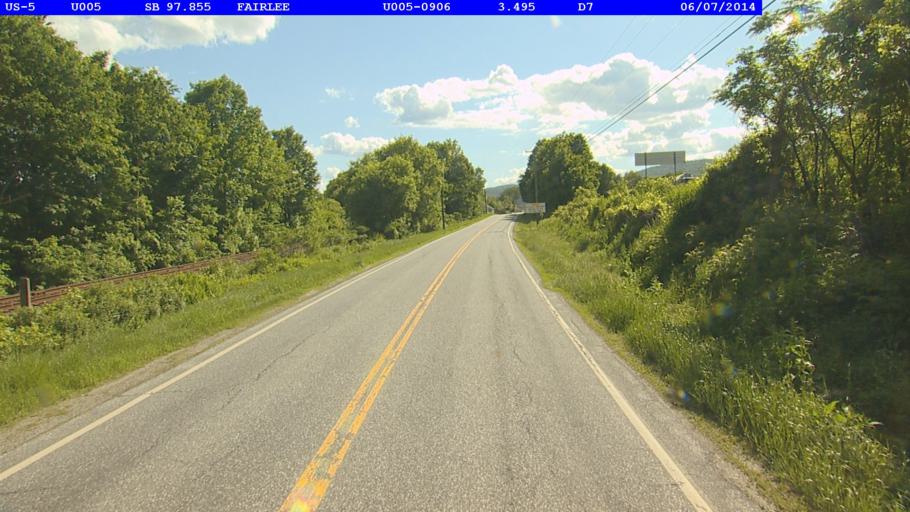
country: US
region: New Hampshire
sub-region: Grafton County
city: Orford
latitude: 43.9107
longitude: -72.1366
